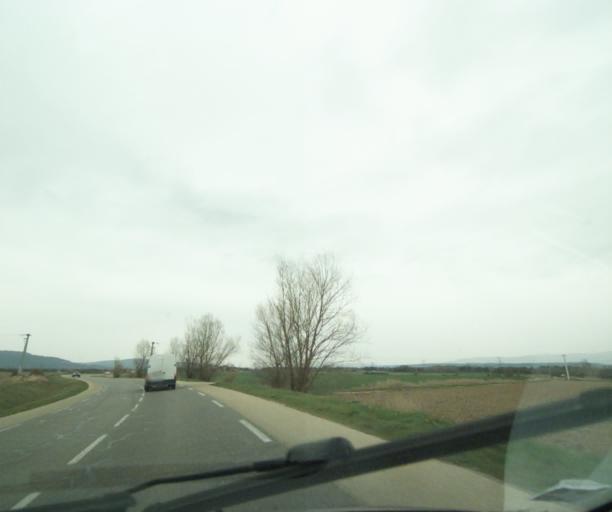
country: FR
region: Provence-Alpes-Cote d'Azur
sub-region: Departement des Bouches-du-Rhone
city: Meyrargues
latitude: 43.6521
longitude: 5.5184
